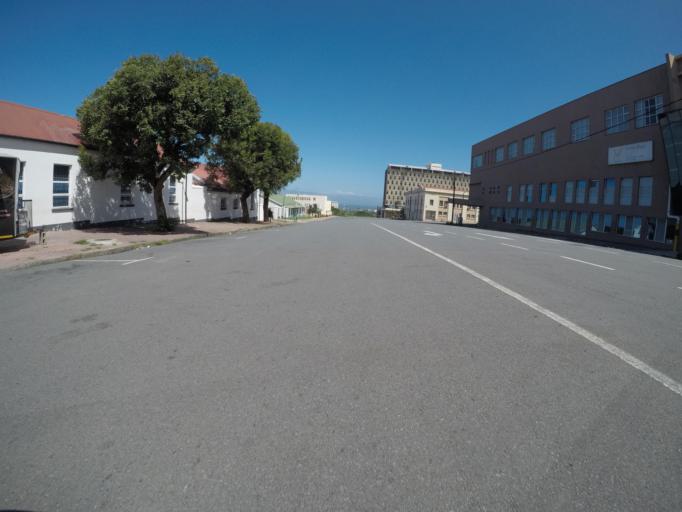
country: ZA
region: Eastern Cape
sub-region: Buffalo City Metropolitan Municipality
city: East London
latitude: -33.0194
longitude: 27.9072
